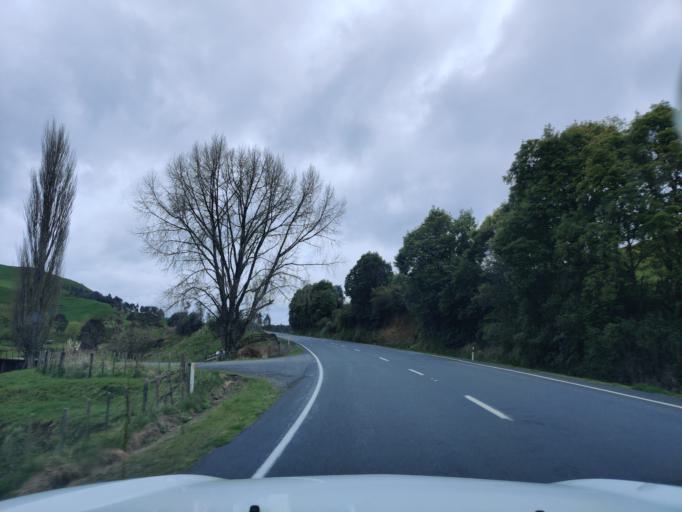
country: NZ
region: Waikato
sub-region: Otorohanga District
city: Otorohanga
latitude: -38.5369
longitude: 175.1783
